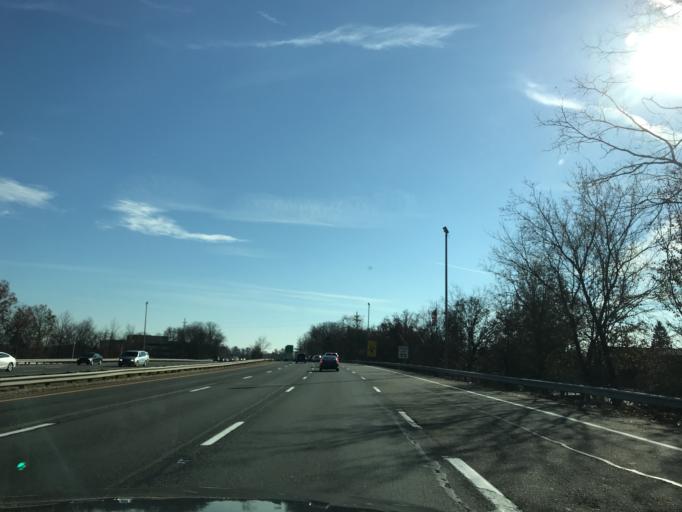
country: US
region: New Jersey
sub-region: Morris County
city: Parsippany
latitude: 40.8728
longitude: -74.4205
